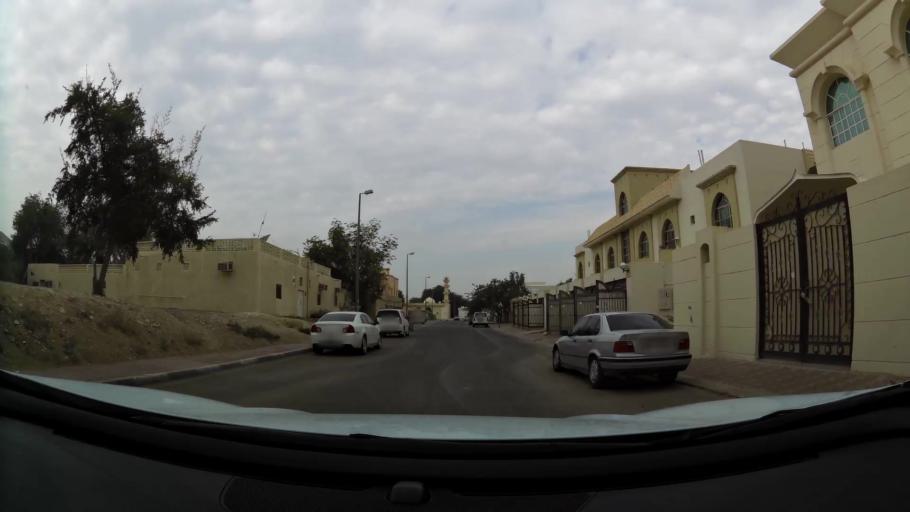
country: AE
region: Abu Dhabi
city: Al Ain
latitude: 24.2264
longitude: 55.7351
